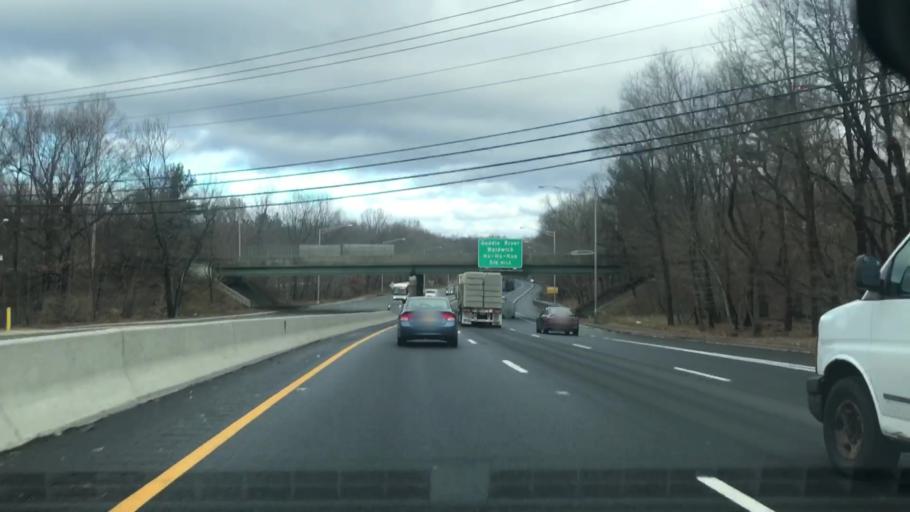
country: US
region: New Jersey
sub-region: Bergen County
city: Ho-Ho-Kus
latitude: 41.0010
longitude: -74.1011
